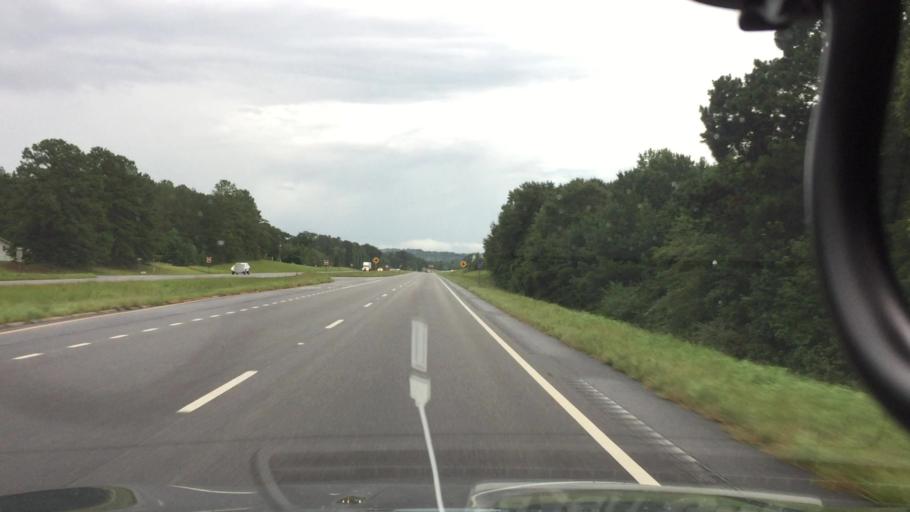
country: US
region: Alabama
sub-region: Pike County
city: Troy
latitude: 31.8794
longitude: -86.0045
